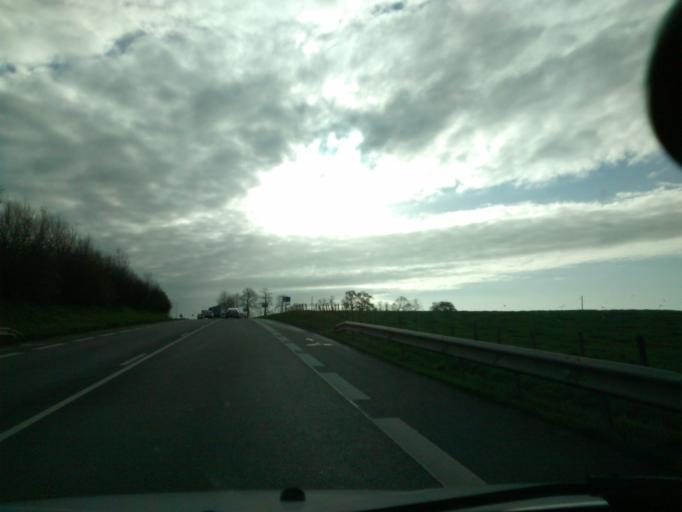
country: FR
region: Brittany
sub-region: Departement d'Ille-et-Vilaine
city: Vitre
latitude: 48.1155
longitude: -1.2280
